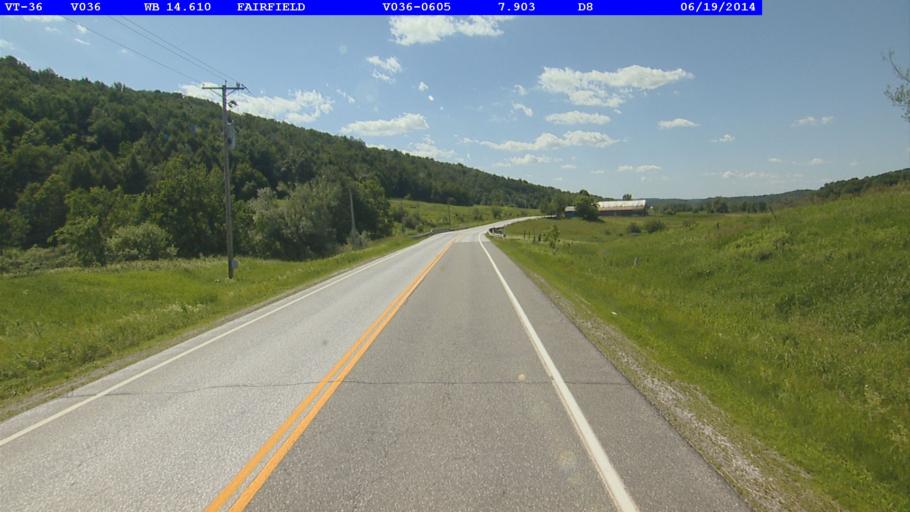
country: US
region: Vermont
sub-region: Franklin County
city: Enosburg Falls
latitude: 44.7963
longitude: -72.8840
